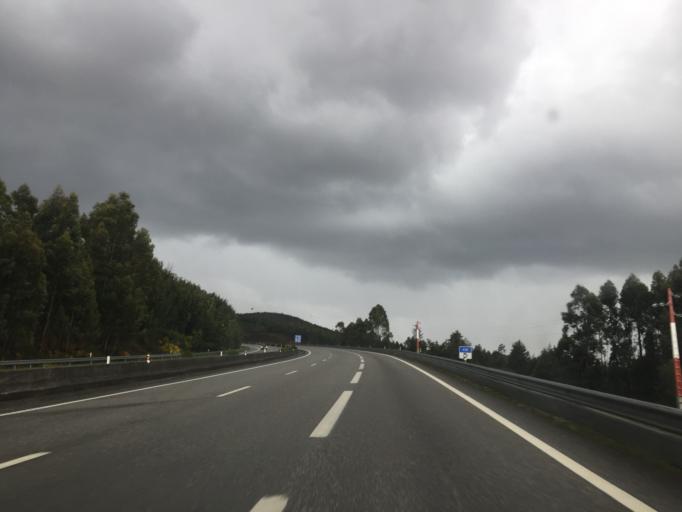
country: PT
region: Aveiro
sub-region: Agueda
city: Valongo
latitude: 40.6626
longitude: -8.3935
